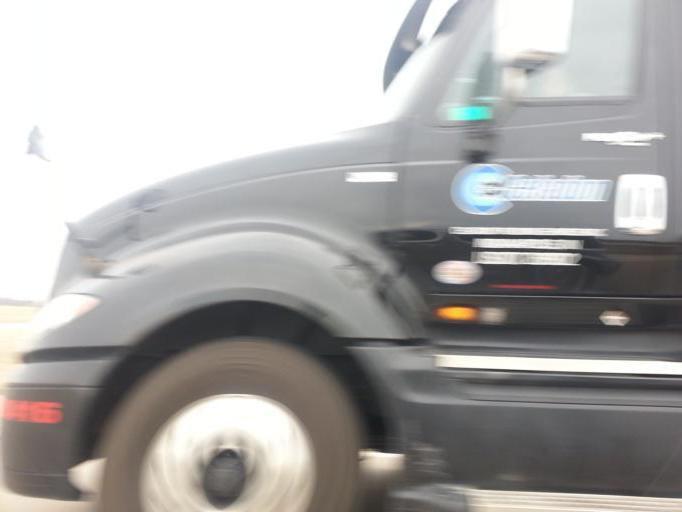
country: US
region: Illinois
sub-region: Woodford County
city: El Paso
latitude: 40.7970
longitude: -89.0353
